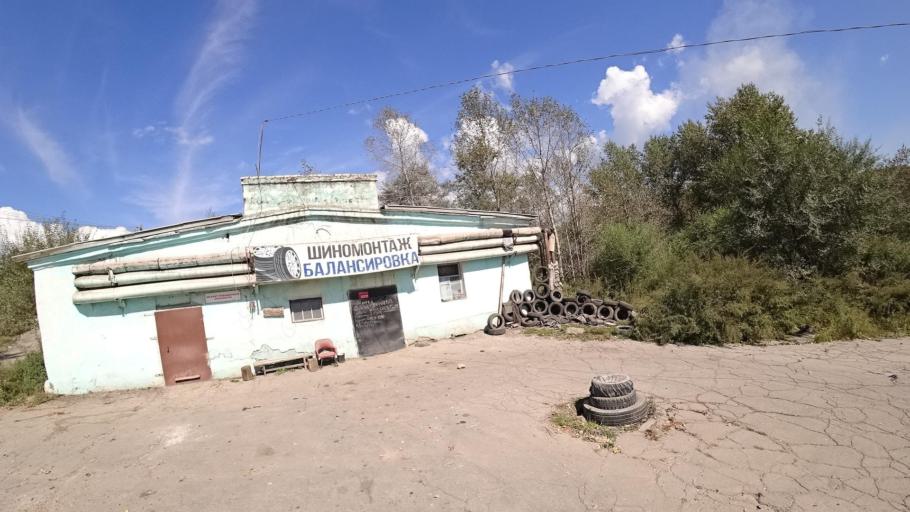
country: RU
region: Jewish Autonomous Oblast
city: Londoko
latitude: 49.0059
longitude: 131.8860
